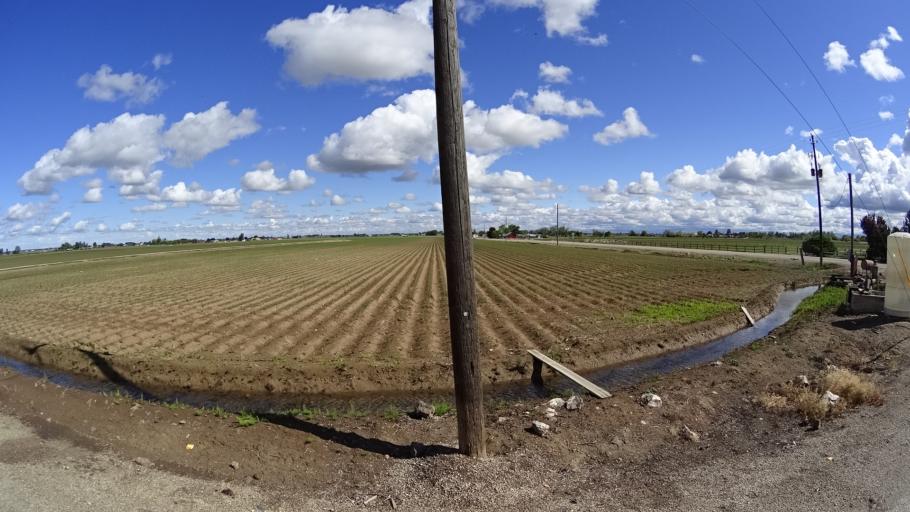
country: US
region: Idaho
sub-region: Ada County
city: Kuna
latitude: 43.4665
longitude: -116.4540
